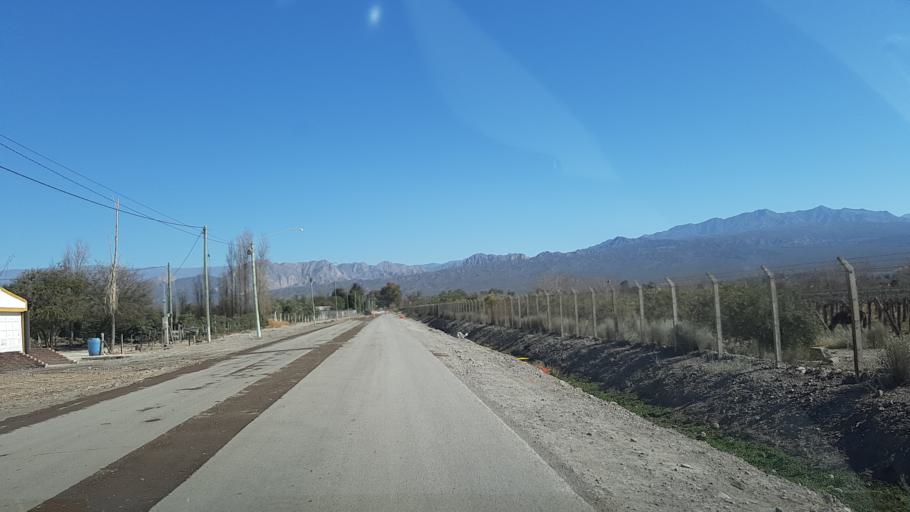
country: AR
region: San Juan
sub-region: Departamento de Zonda
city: Zonda
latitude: -31.4692
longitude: -68.7272
